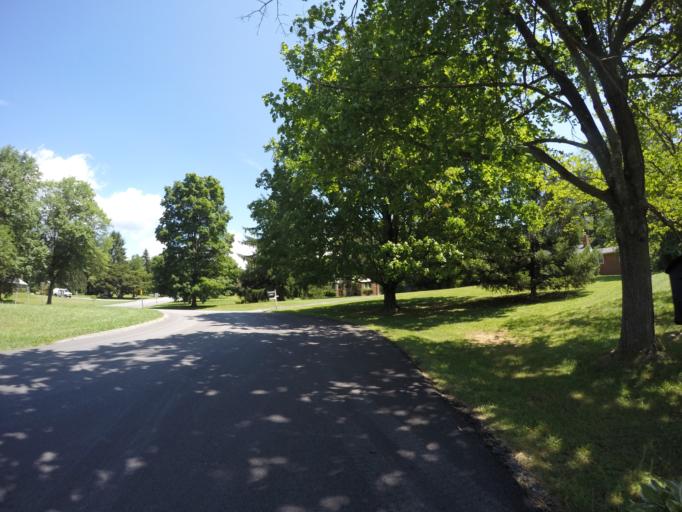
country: US
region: Maryland
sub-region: Howard County
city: Columbia
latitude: 39.2784
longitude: -76.8733
